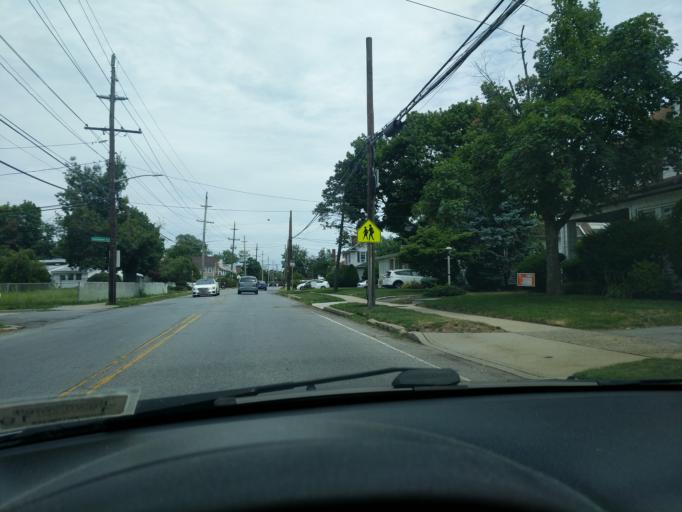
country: US
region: New York
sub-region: Nassau County
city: Woodmere
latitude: 40.6351
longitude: -73.7112
